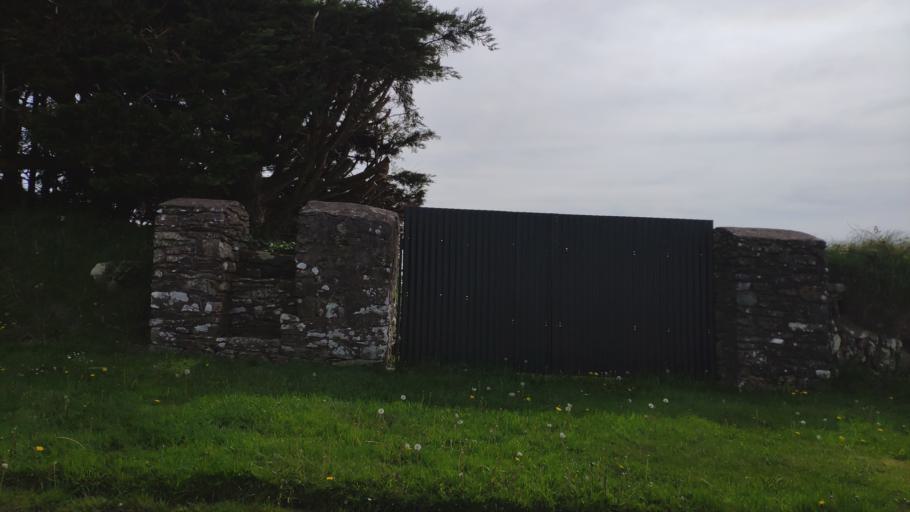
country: IE
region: Munster
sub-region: County Cork
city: Blarney
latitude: 51.9693
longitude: -8.5135
